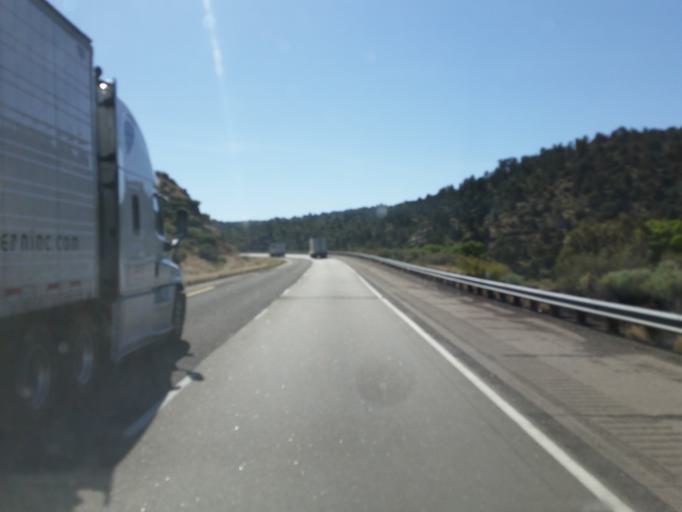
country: US
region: Arizona
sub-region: Mohave County
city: Peach Springs
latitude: 35.1770
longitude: -113.4808
